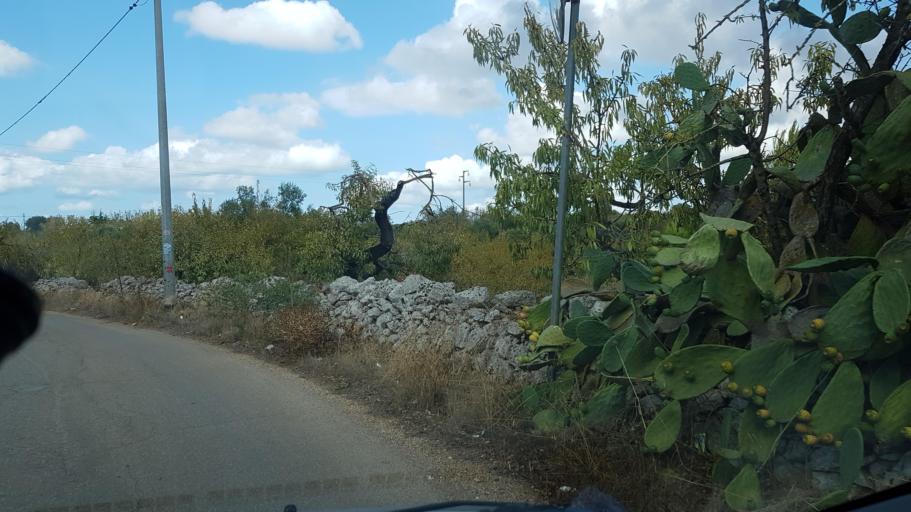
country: IT
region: Apulia
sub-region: Provincia di Brindisi
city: San Vito dei Normanni
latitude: 40.6685
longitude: 17.7170
